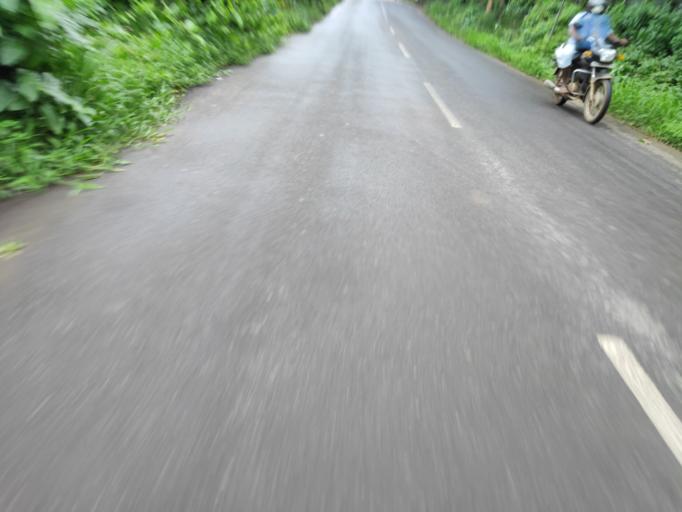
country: IN
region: Kerala
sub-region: Malappuram
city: Manjeri
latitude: 11.2259
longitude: 76.2703
